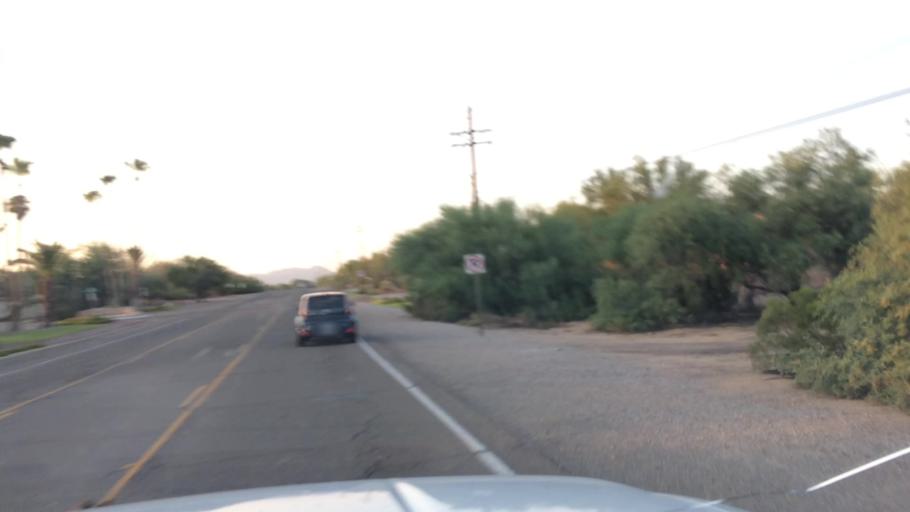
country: US
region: Arizona
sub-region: Pima County
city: Casas Adobes
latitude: 32.3410
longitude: -111.0205
